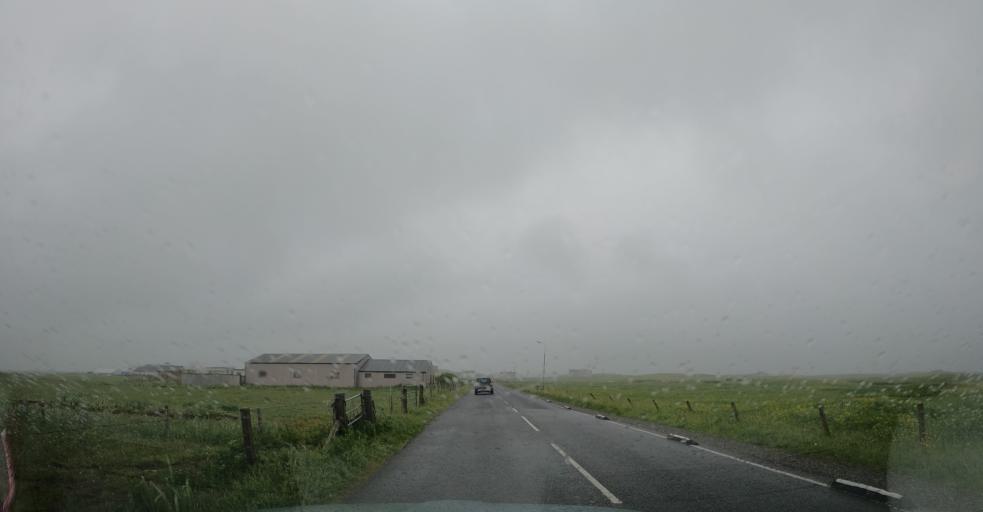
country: GB
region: Scotland
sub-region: Eilean Siar
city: Benbecula
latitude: 57.4719
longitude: -7.3680
